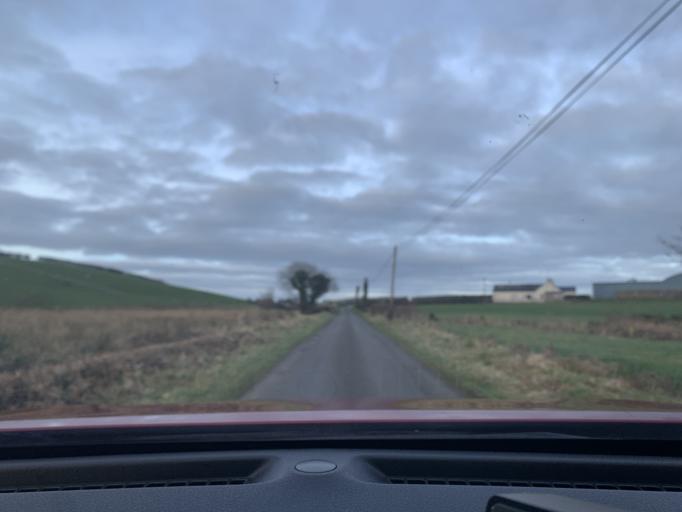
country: IE
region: Connaught
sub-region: Sligo
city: Ballymote
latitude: 54.0516
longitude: -8.5691
